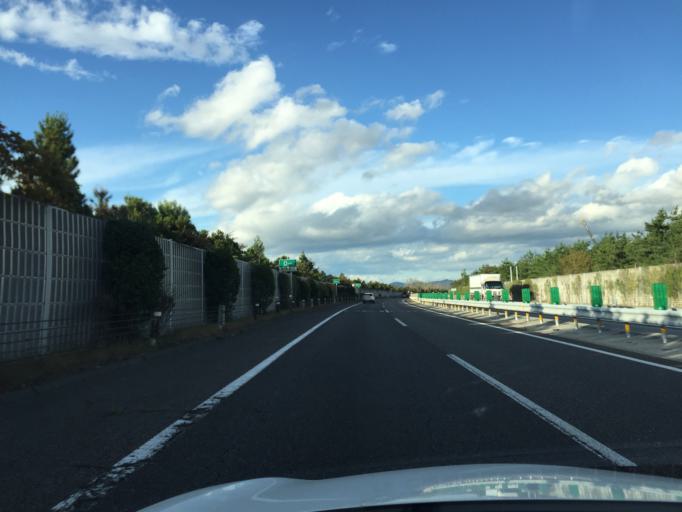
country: JP
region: Fukushima
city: Koriyama
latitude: 37.3977
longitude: 140.3105
